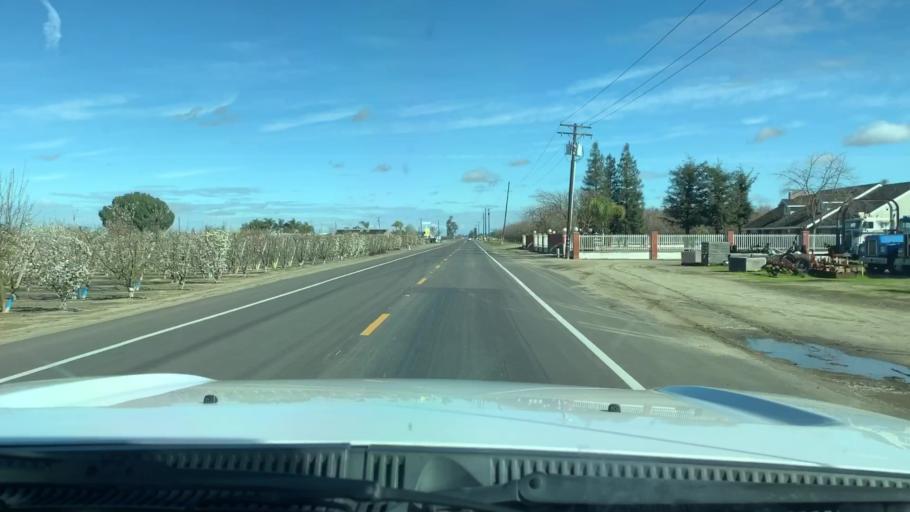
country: US
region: California
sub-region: Fresno County
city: Laton
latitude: 36.5006
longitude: -119.6830
